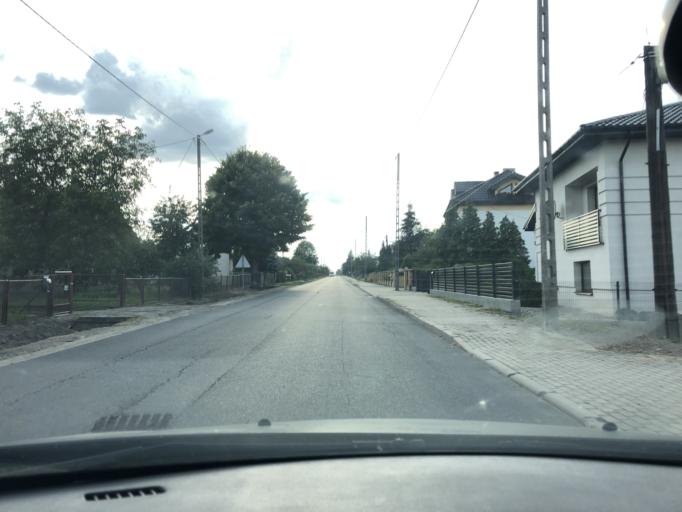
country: PL
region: Lodz Voivodeship
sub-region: Powiat wieruszowski
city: Walichnowy
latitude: 51.2620
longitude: 18.4148
